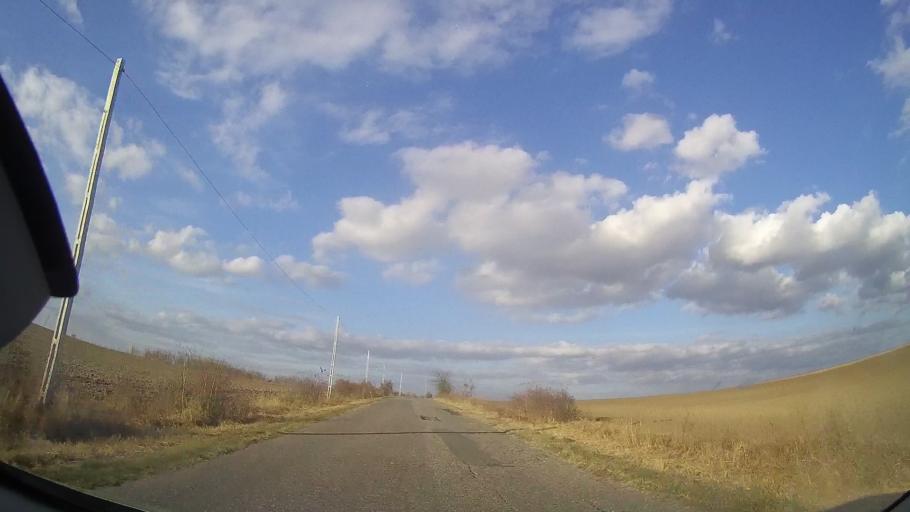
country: RO
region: Constanta
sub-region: Comuna Cerchezu
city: Cerchezu
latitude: 43.8447
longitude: 28.0985
